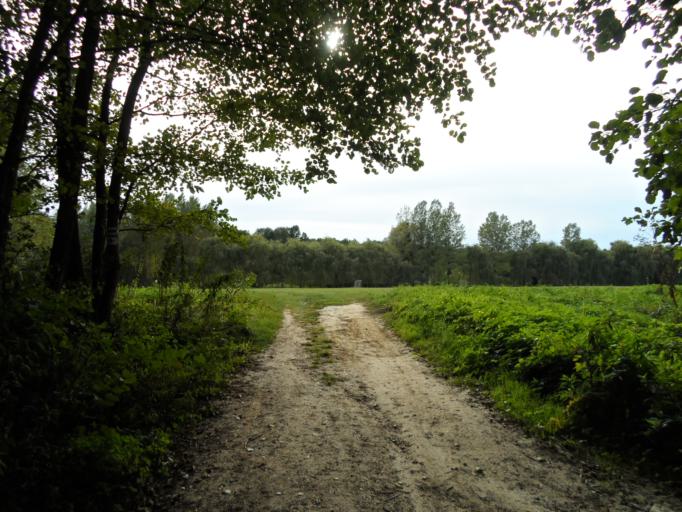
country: HU
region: Veszprem
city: Ajka
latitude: 47.2236
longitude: 17.5538
